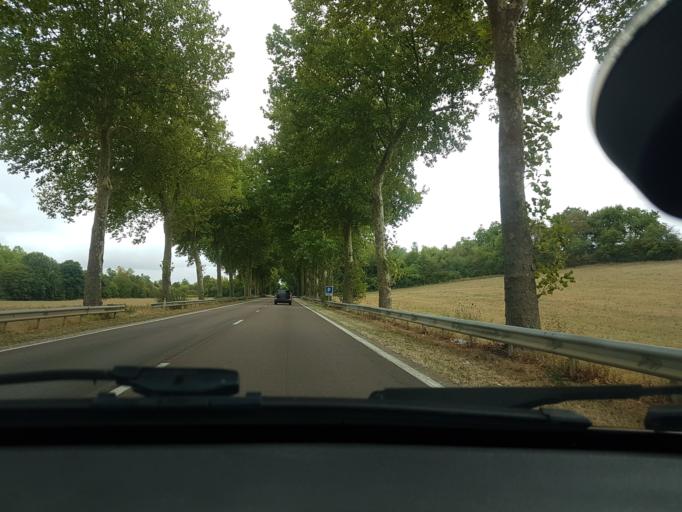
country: FR
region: Bourgogne
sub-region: Departement de l'Yonne
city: Champs-sur-Yonne
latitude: 47.7142
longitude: 3.6195
